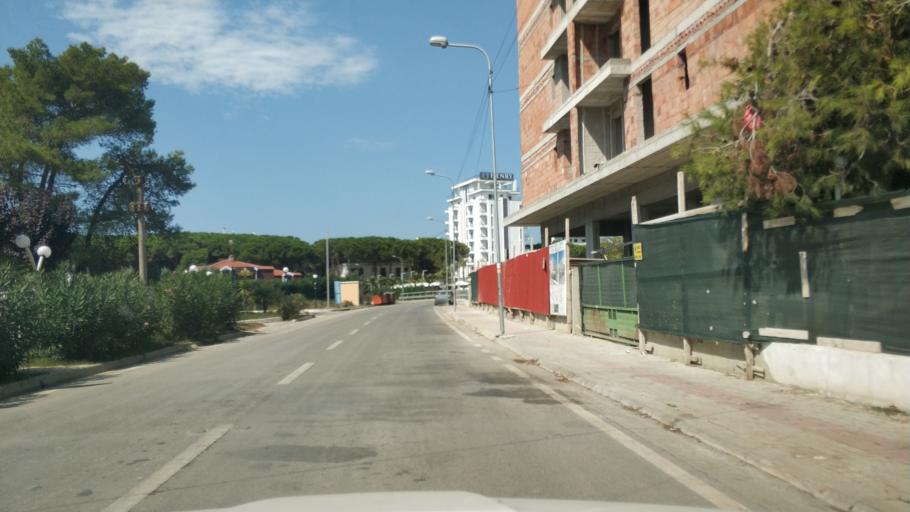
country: AL
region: Tirane
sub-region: Rrethi i Kavajes
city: Golem
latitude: 41.2377
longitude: 19.5203
